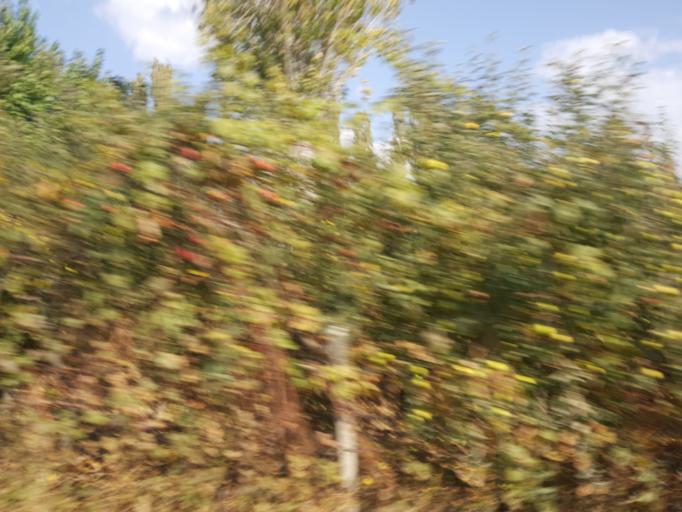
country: TR
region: Corum
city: Sungurlu
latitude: 40.1820
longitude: 34.4915
